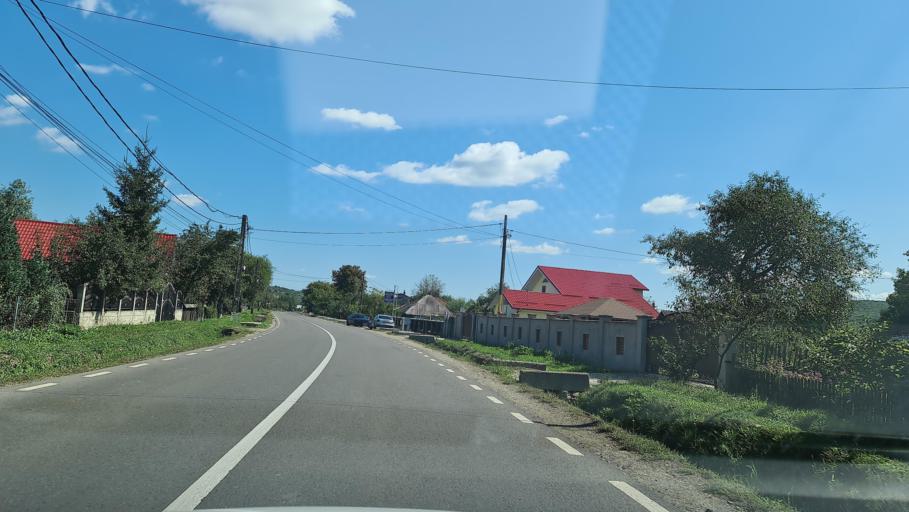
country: RO
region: Bacau
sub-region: Comuna Ardeoani
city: Ardeoani
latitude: 46.5324
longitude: 26.6275
